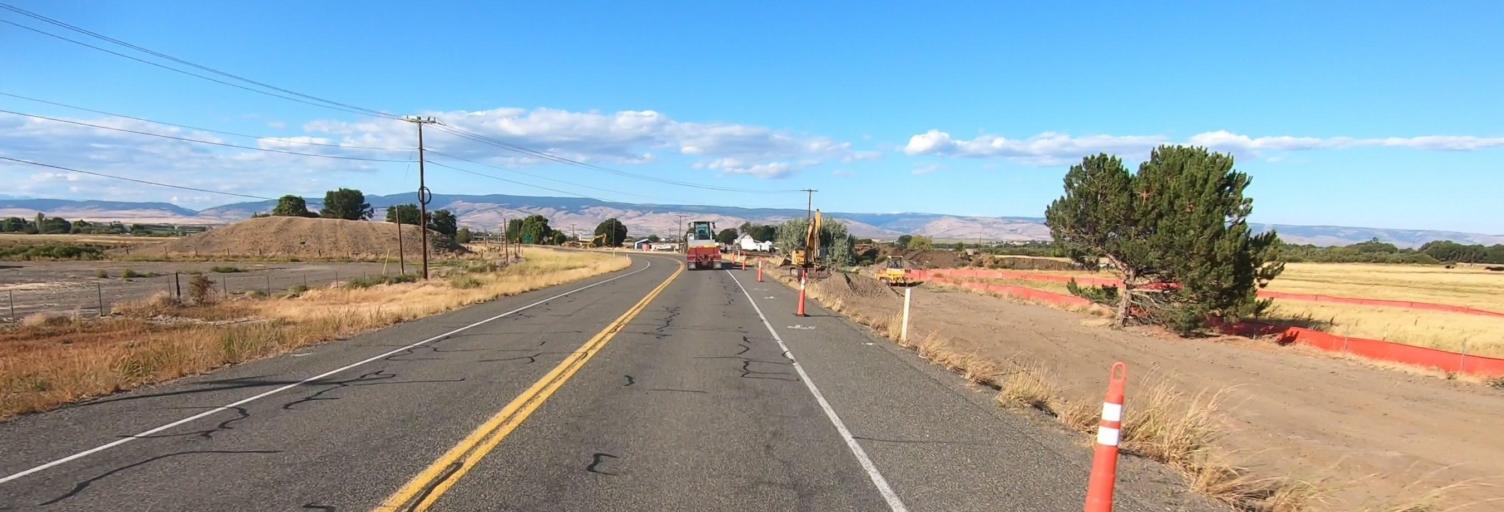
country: US
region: Washington
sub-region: Kittitas County
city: Ellensburg
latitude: 47.0161
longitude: -120.5993
